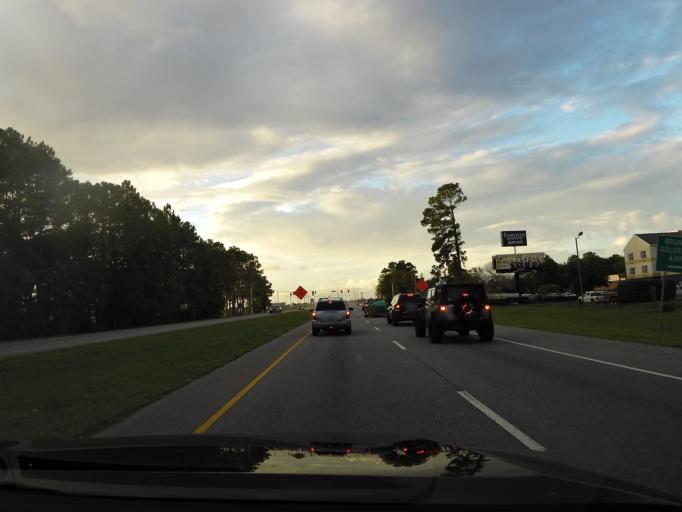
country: US
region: Georgia
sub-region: Glynn County
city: Dock Junction
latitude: 31.2355
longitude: -81.5002
